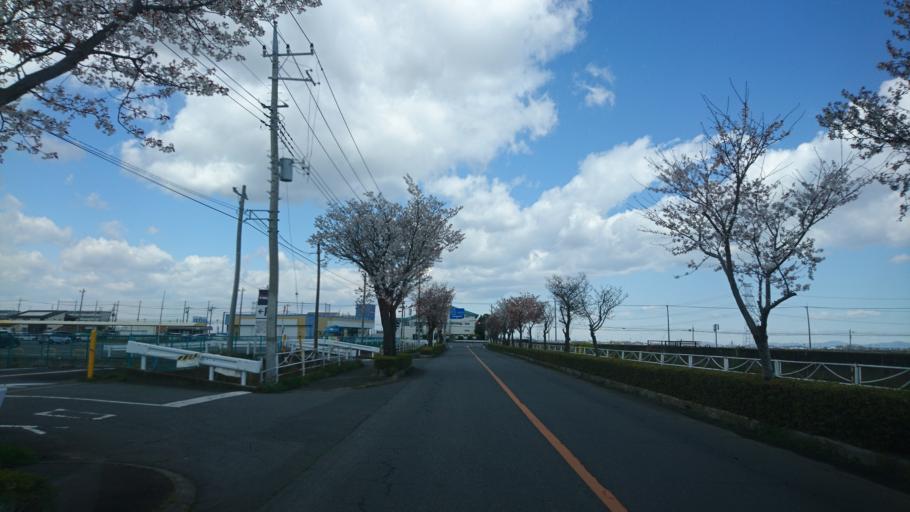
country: JP
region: Ibaraki
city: Ishige
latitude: 36.1203
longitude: 139.9772
